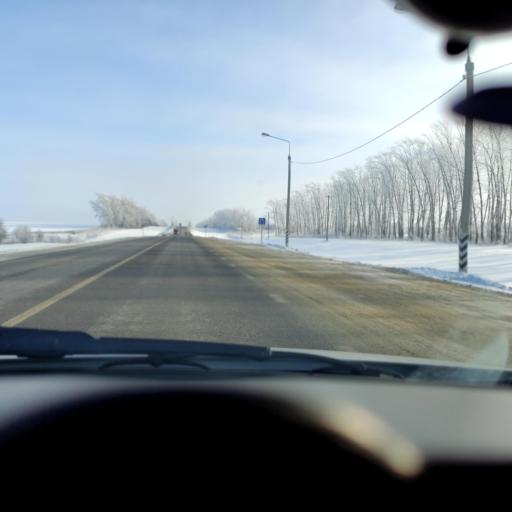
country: RU
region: Kursk
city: Kshenskiy
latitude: 51.6205
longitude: 37.5931
